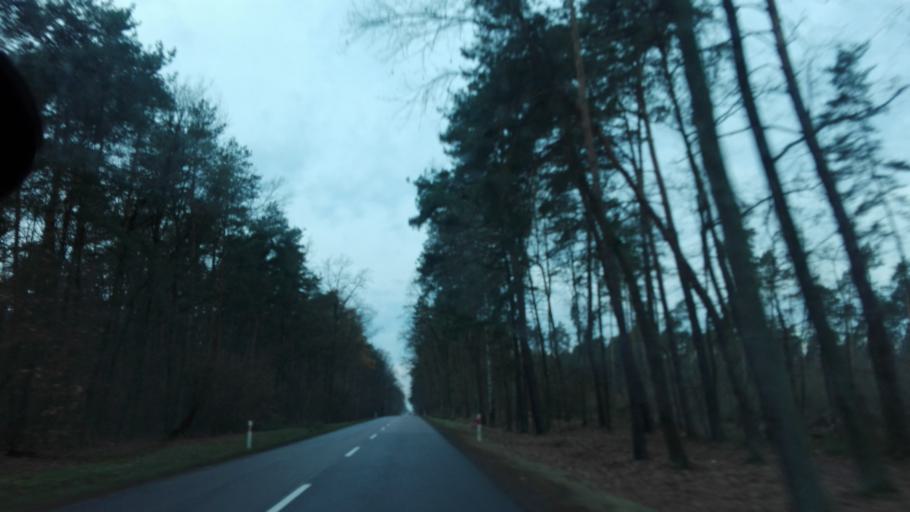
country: PL
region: Lublin Voivodeship
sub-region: Powiat radzynski
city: Radzyn Podlaski
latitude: 51.7776
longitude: 22.6745
